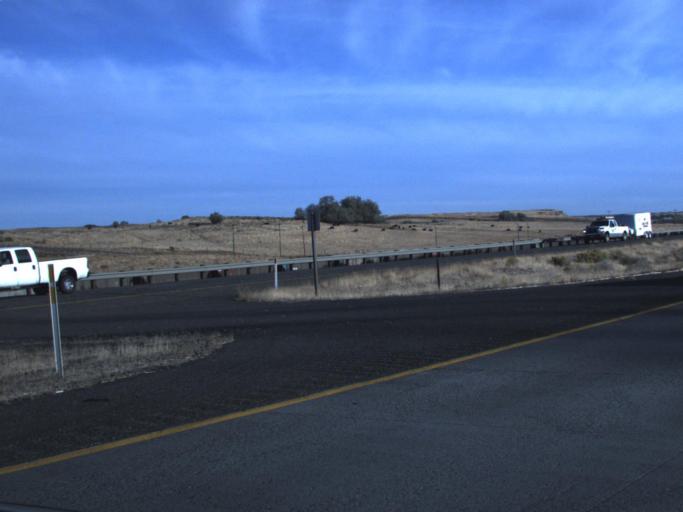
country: US
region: Washington
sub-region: Franklin County
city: Basin City
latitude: 46.5444
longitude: -119.0078
